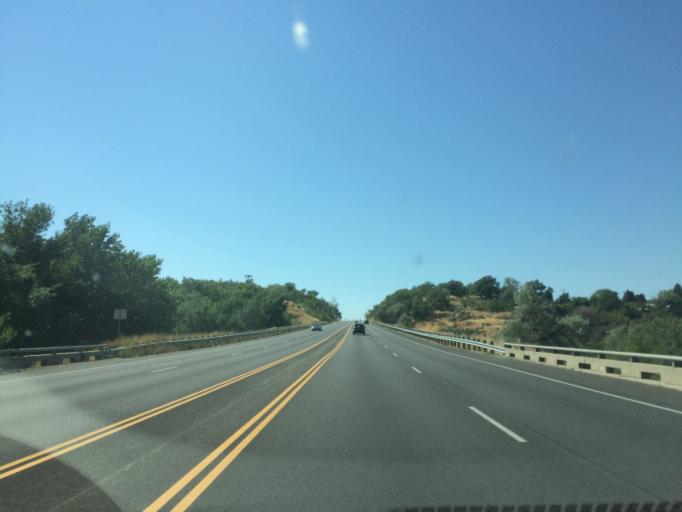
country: US
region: Utah
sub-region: Weber County
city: Ogden
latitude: 41.2370
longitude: -111.9462
